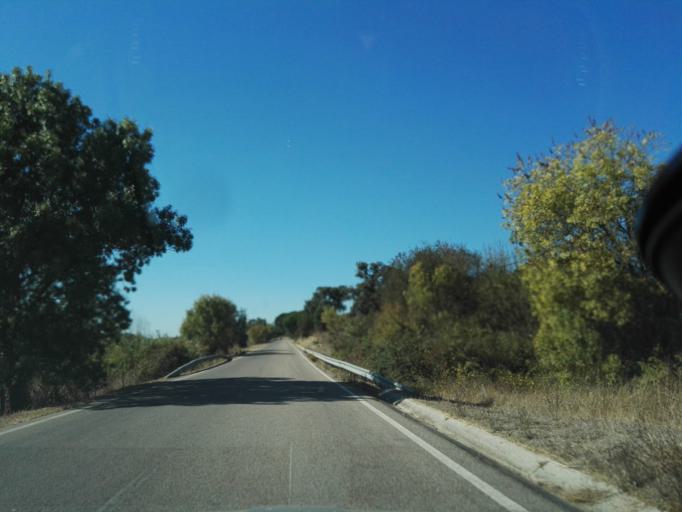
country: PT
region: Santarem
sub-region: Benavente
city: Poceirao
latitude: 38.8520
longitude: -8.7222
